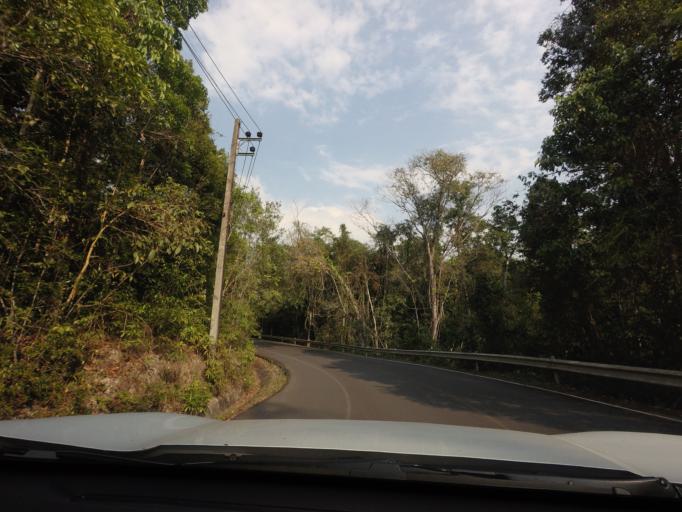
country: TH
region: Nakhon Ratchasima
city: Pak Chong
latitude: 14.4252
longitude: 101.3932
